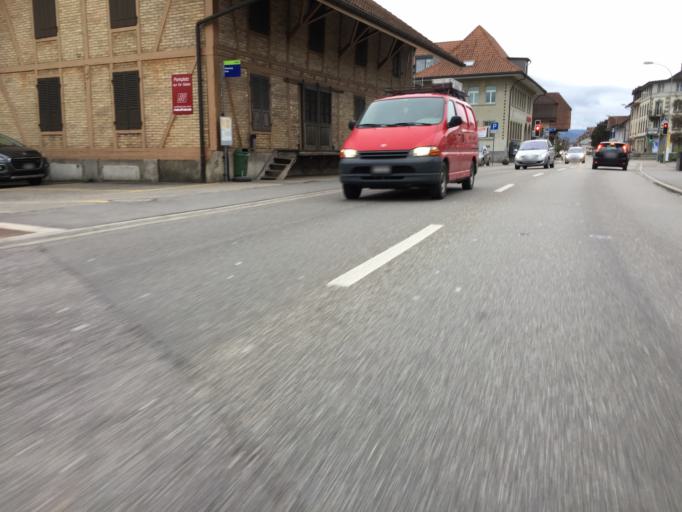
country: CH
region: Bern
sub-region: Emmental District
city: Oberburg
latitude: 47.0401
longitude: 7.6249
